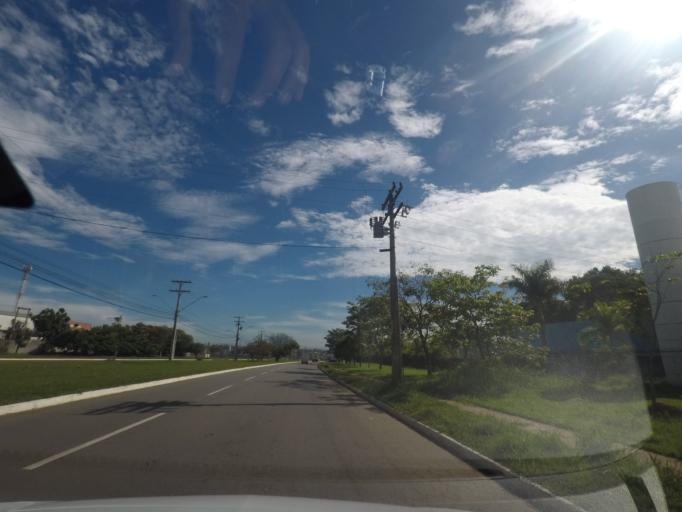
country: BR
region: Goias
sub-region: Aparecida De Goiania
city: Aparecida de Goiania
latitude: -16.7925
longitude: -49.2532
